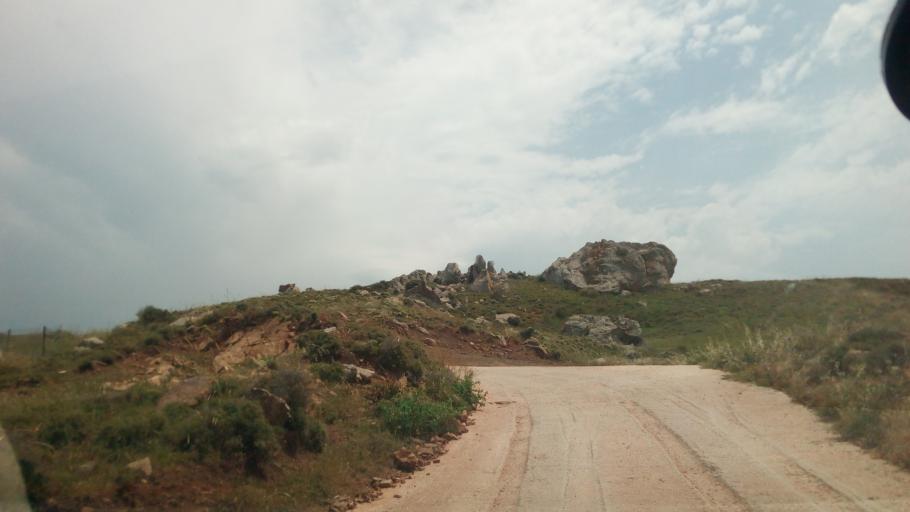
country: CY
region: Pafos
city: Polis
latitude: 34.9827
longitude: 32.3528
